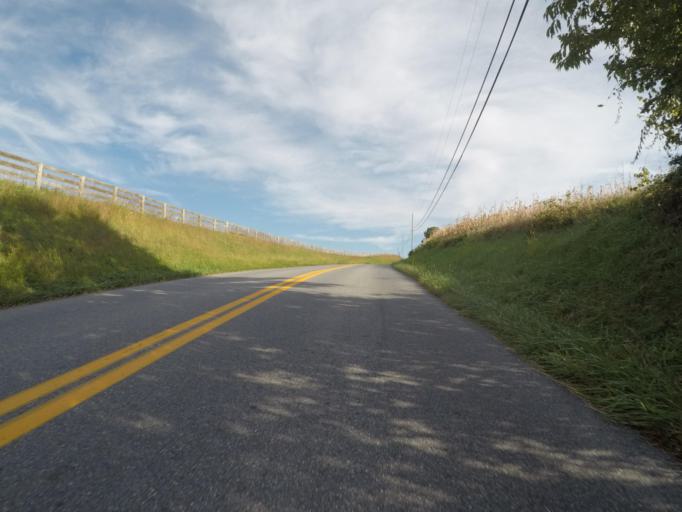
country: US
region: Maryland
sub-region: Baltimore County
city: Reisterstown
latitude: 39.5389
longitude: -76.7885
